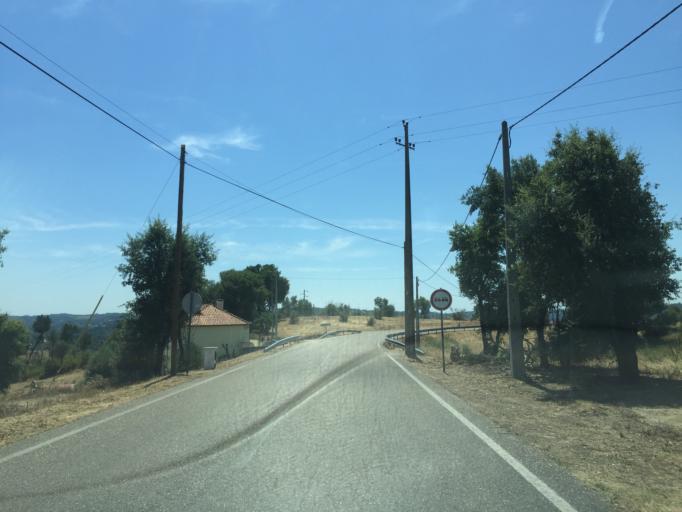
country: PT
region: Santarem
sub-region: Constancia
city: Constancia
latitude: 39.5761
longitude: -8.2952
